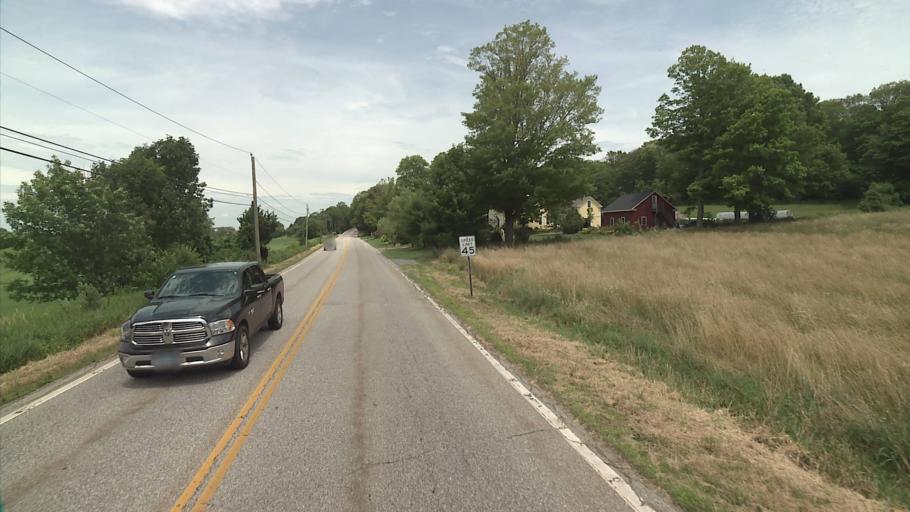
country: US
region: Connecticut
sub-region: New London County
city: Preston City
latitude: 41.5351
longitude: -71.9697
